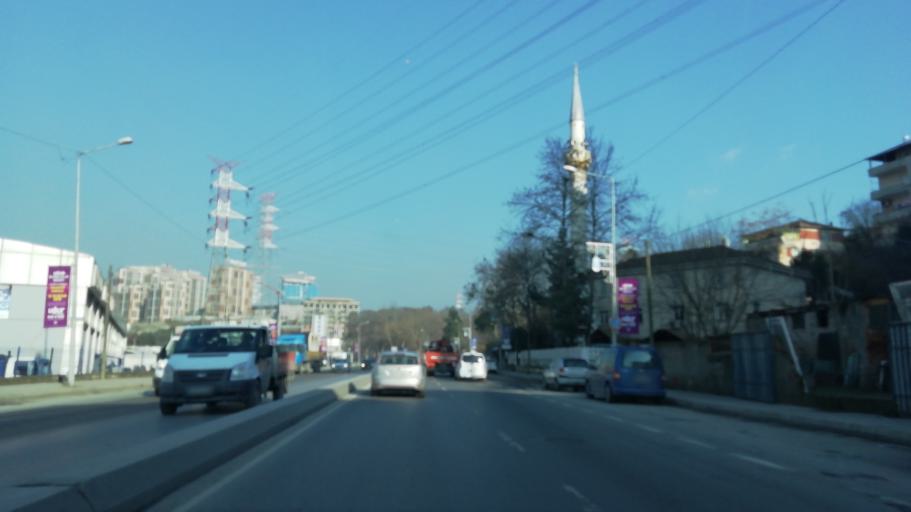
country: TR
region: Istanbul
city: Sisli
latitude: 41.0818
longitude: 28.9517
